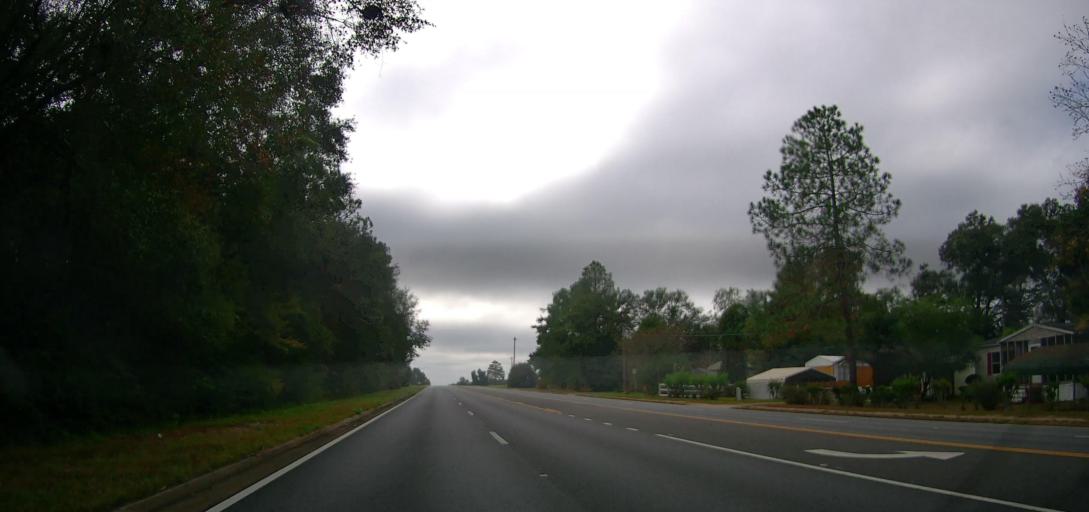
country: US
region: Georgia
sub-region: Thomas County
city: Thomasville
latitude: 31.0001
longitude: -83.8707
